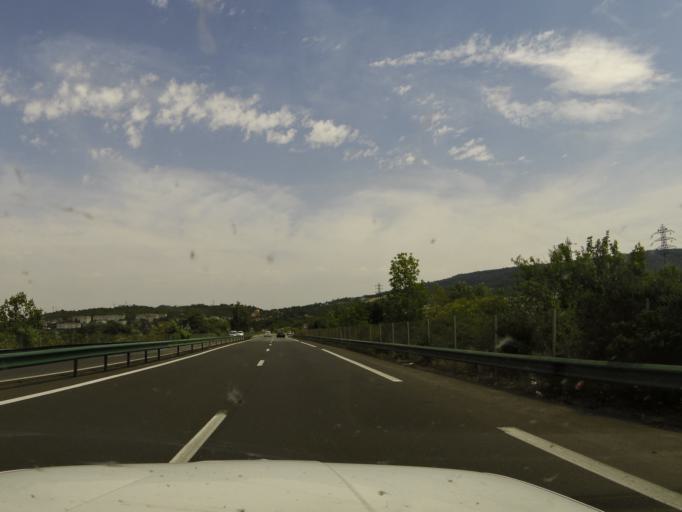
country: FR
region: Auvergne
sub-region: Departement du Puy-de-Dome
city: Beaumont
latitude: 45.7471
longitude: 3.0953
